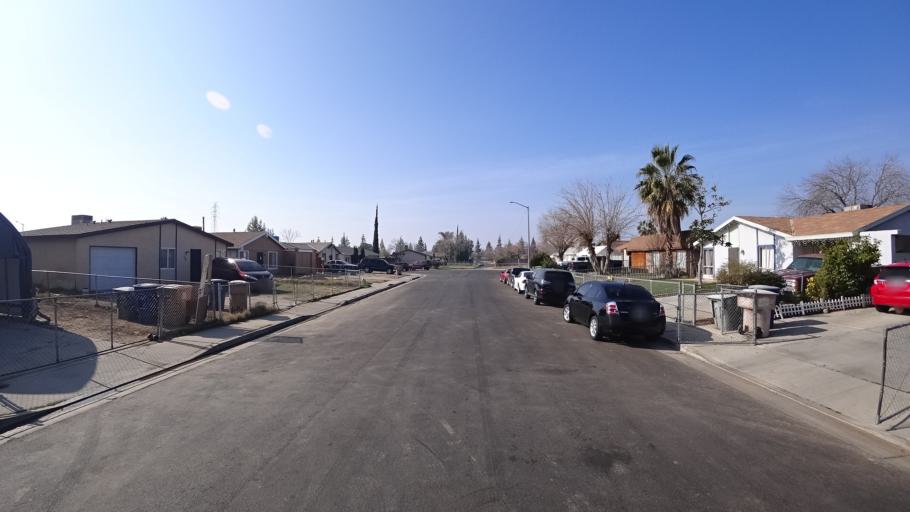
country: US
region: California
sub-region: Kern County
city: Bakersfield
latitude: 35.3194
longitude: -119.0586
